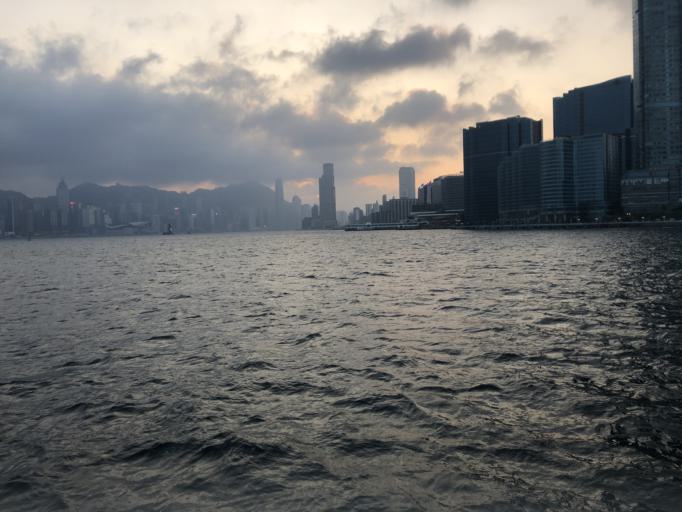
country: HK
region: Kowloon City
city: Kowloon
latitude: 22.3026
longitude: 114.1969
